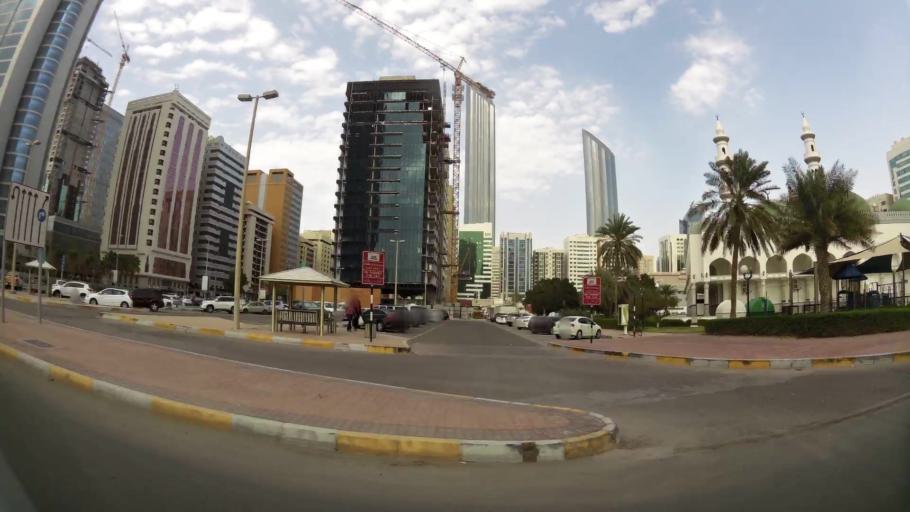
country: AE
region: Abu Dhabi
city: Abu Dhabi
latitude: 24.4842
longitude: 54.3518
